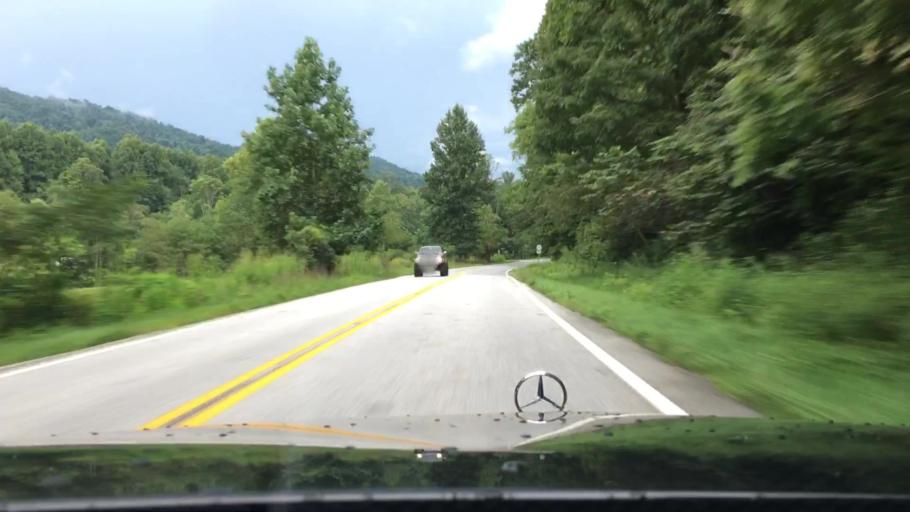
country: US
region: Virginia
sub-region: Nelson County
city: Lovingston
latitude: 37.8186
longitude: -78.9362
